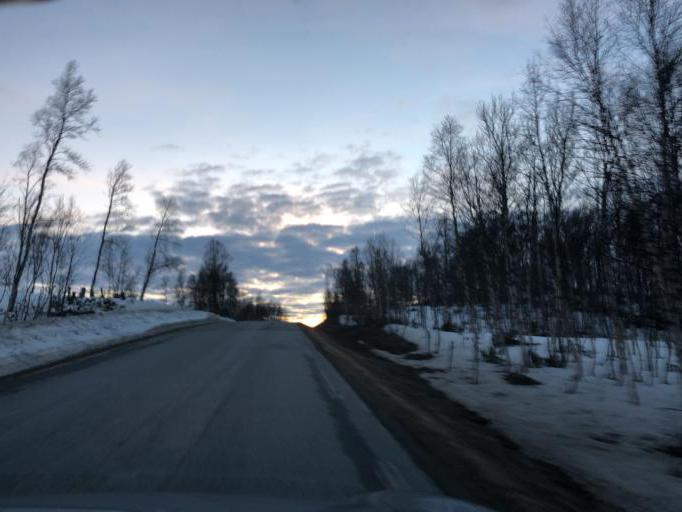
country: NO
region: Sor-Trondelag
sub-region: Tydal
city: Aas
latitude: 62.6813
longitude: 11.7803
